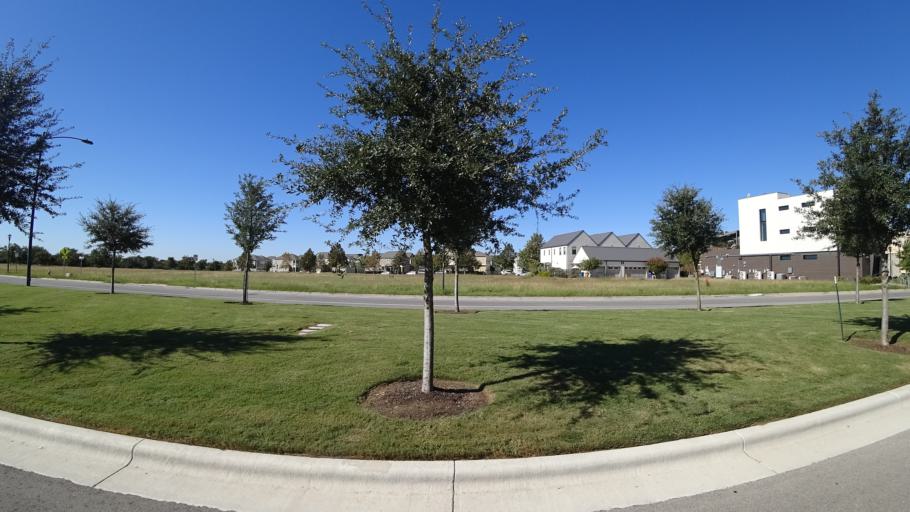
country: US
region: Texas
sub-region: Travis County
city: Austin
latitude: 30.2915
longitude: -97.6990
